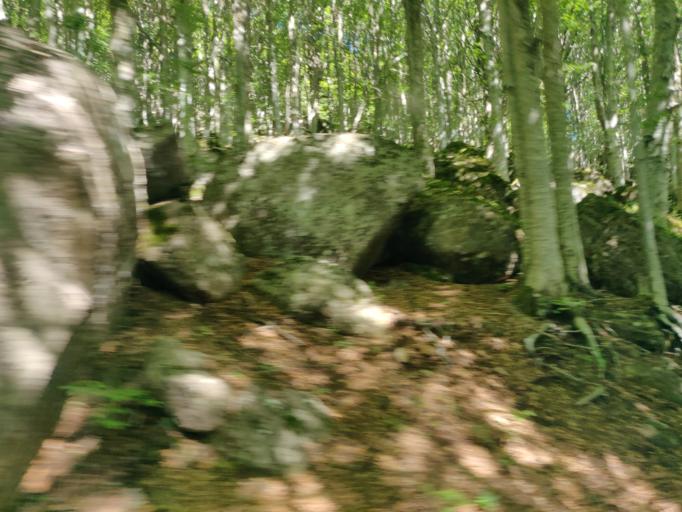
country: IT
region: Tuscany
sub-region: Provincia di Siena
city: Abbadia San Salvatore
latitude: 42.8846
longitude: 11.6249
